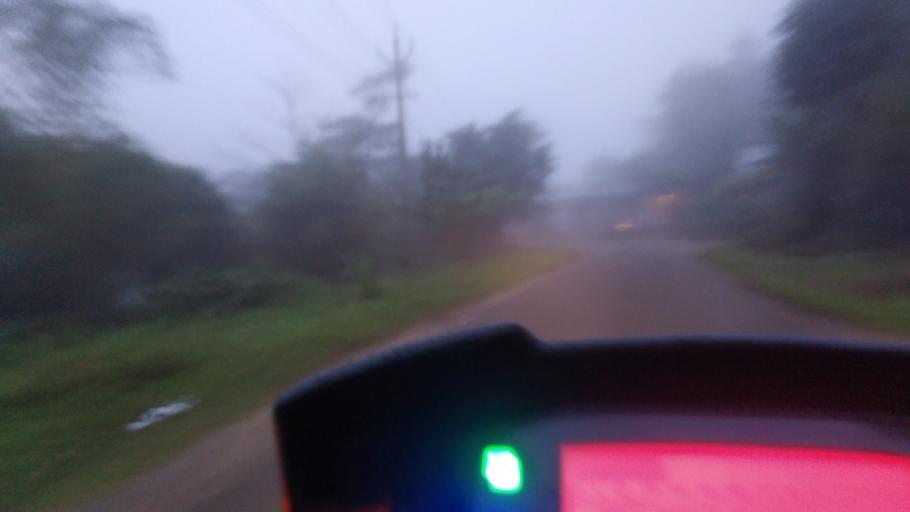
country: IN
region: Kerala
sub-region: Kottayam
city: Erattupetta
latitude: 9.5361
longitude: 76.9706
